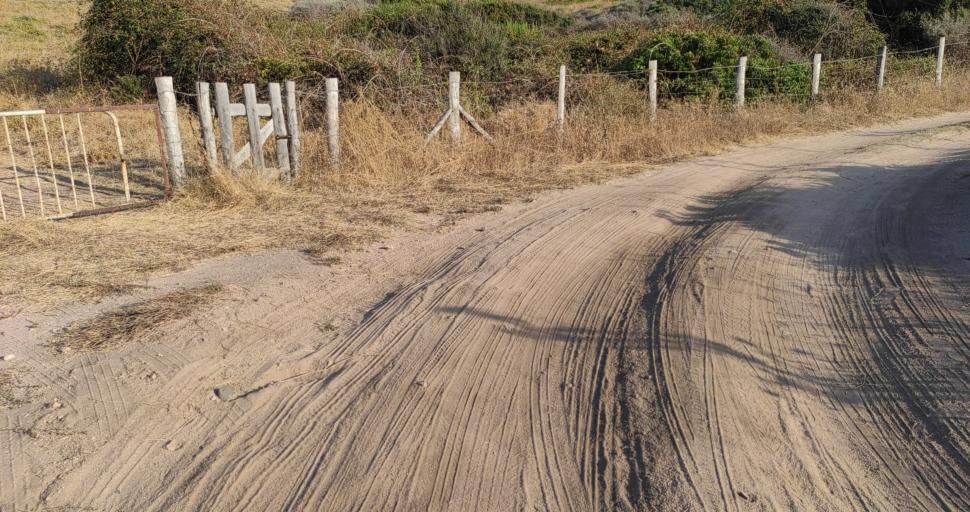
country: FR
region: Corsica
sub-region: Departement de la Corse-du-Sud
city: Alata
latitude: 41.9877
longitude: 8.6714
